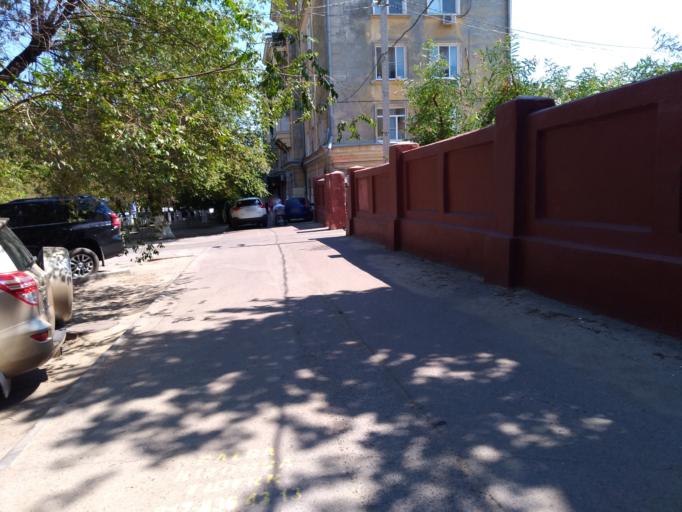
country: RU
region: Volgograd
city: Volgograd
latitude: 48.7147
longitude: 44.5224
